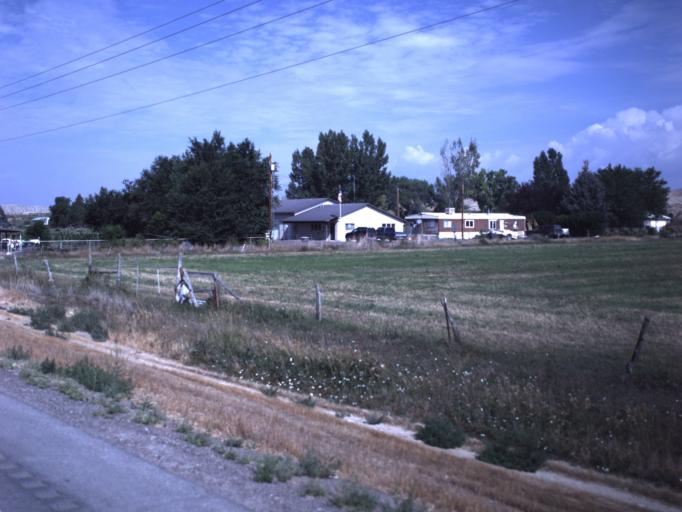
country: US
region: Utah
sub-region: Uintah County
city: Naples
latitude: 40.3696
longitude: -109.3638
